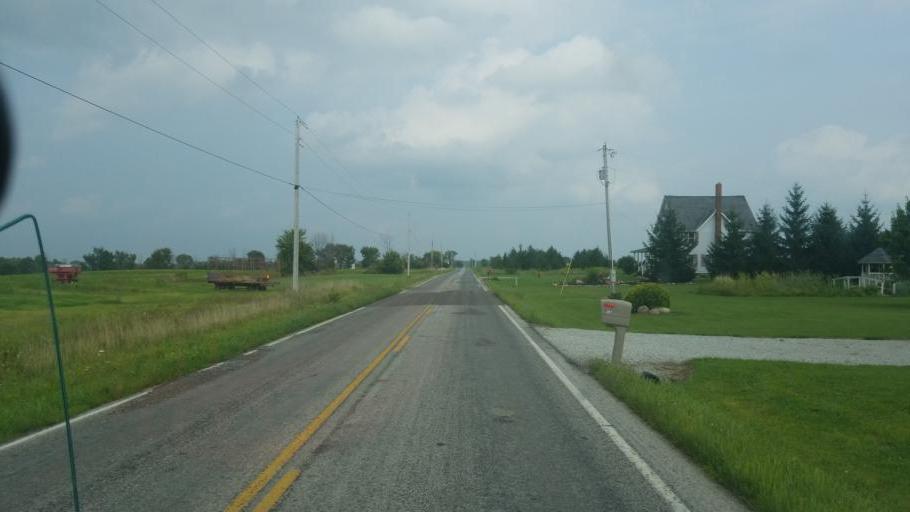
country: US
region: Ohio
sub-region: Lorain County
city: Wellington
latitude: 41.0581
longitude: -82.1967
